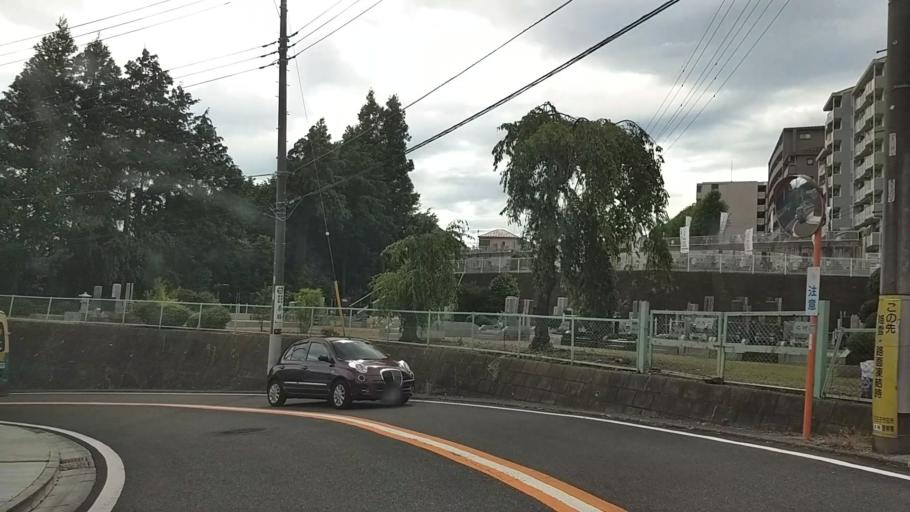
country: JP
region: Tokyo
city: Hachioji
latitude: 35.6369
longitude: 139.2990
